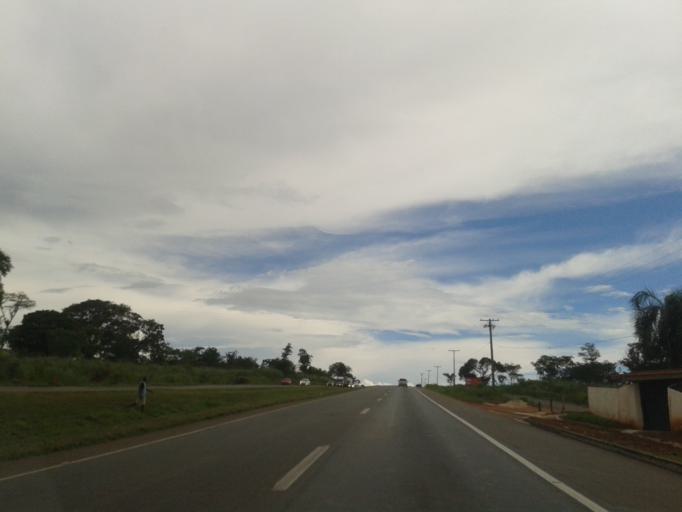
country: BR
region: Goias
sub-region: Aparecida De Goiania
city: Aparecida de Goiania
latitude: -16.8598
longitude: -49.2491
